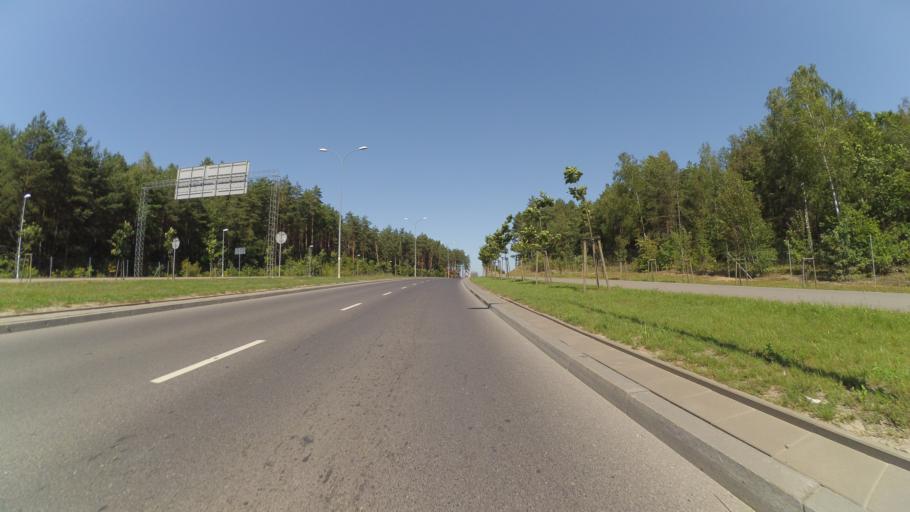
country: PL
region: Podlasie
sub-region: Bialystok
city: Bialystok
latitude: 53.1305
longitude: 23.2225
